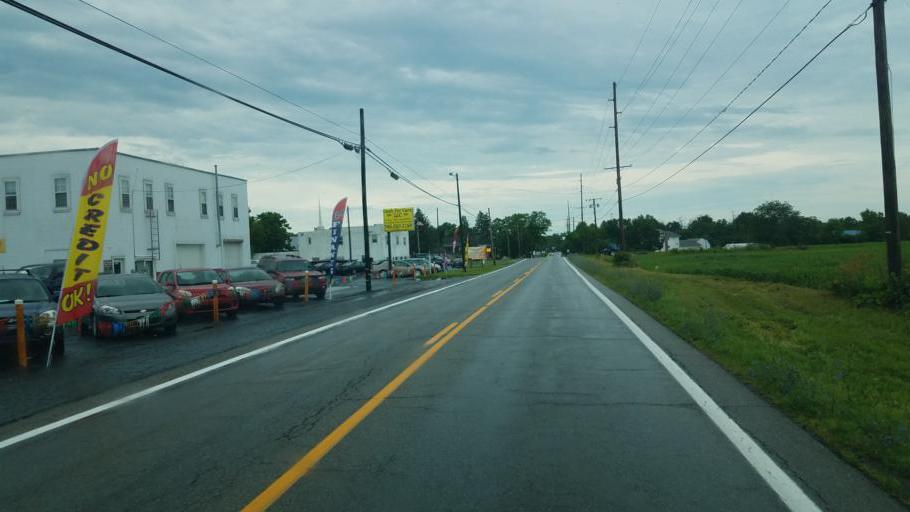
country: US
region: Ohio
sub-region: Marion County
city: Marion
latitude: 40.5610
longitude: -83.1408
